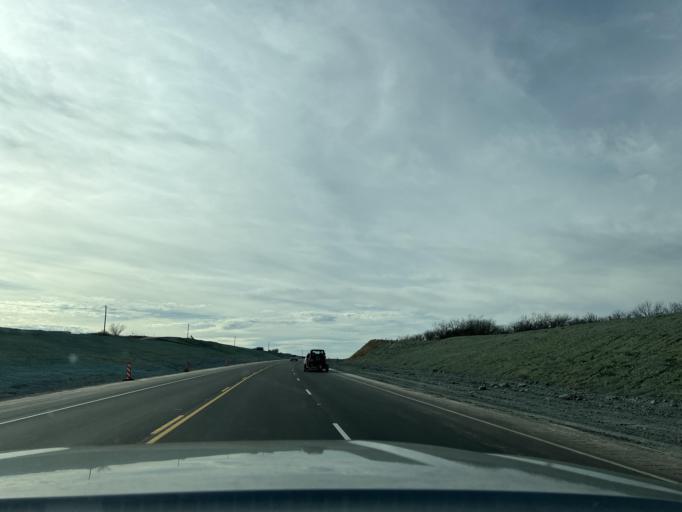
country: US
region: Texas
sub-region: Shackelford County
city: Albany
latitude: 32.7071
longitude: -99.3778
